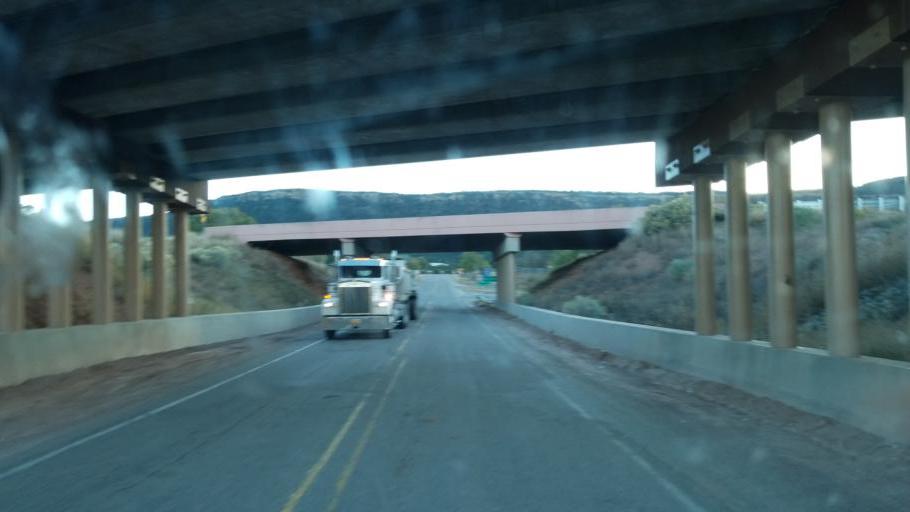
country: US
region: New Mexico
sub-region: San Miguel County
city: Pecos
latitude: 35.4956
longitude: -105.6730
